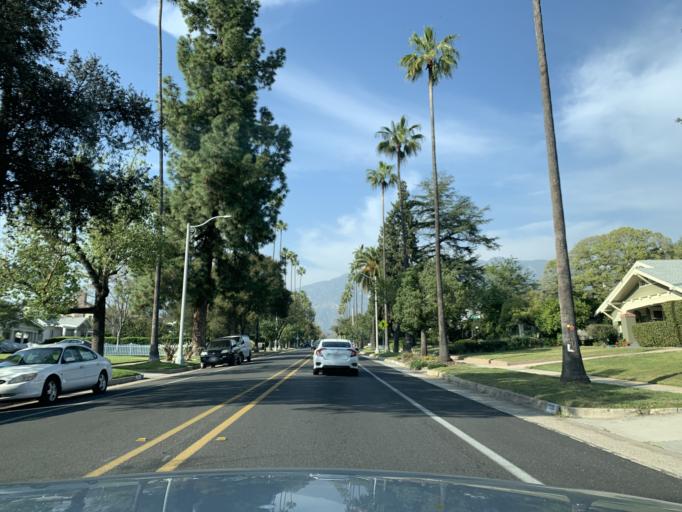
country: US
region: California
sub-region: Los Angeles County
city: Altadena
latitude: 34.1657
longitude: -118.1215
